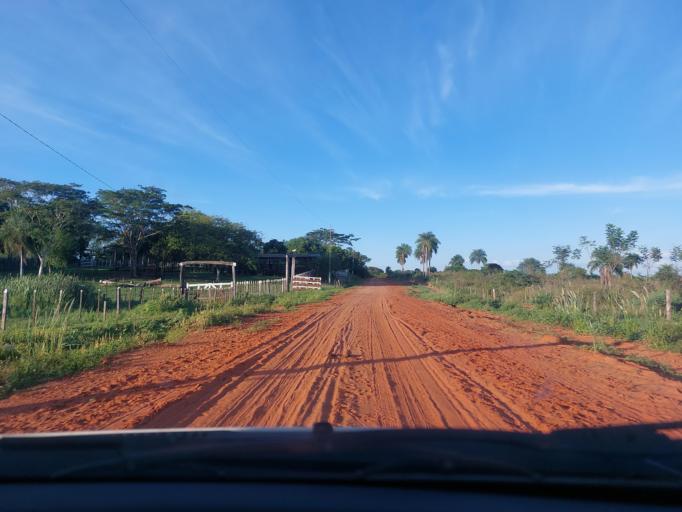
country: PY
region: San Pedro
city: Itacurubi del Rosario
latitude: -24.5495
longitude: -56.5865
